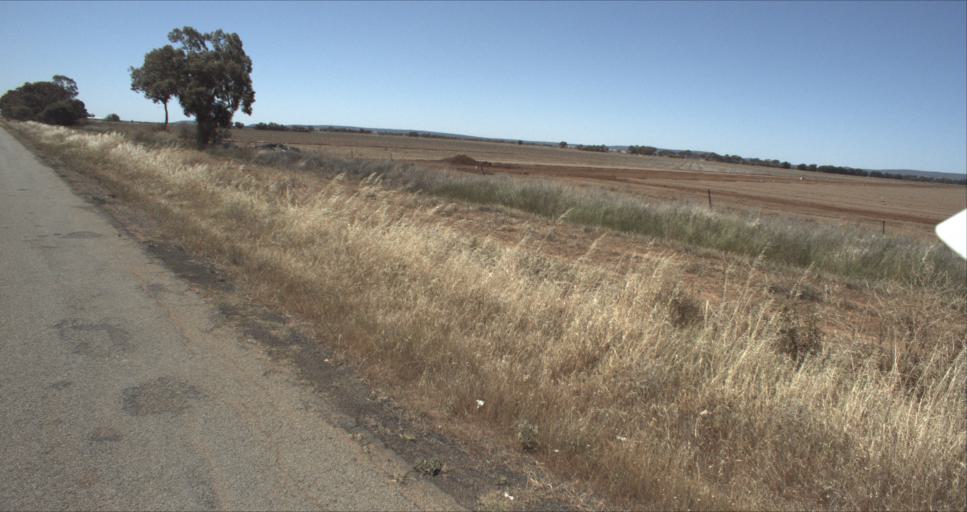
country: AU
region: New South Wales
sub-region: Leeton
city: Leeton
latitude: -34.5166
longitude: 146.3453
